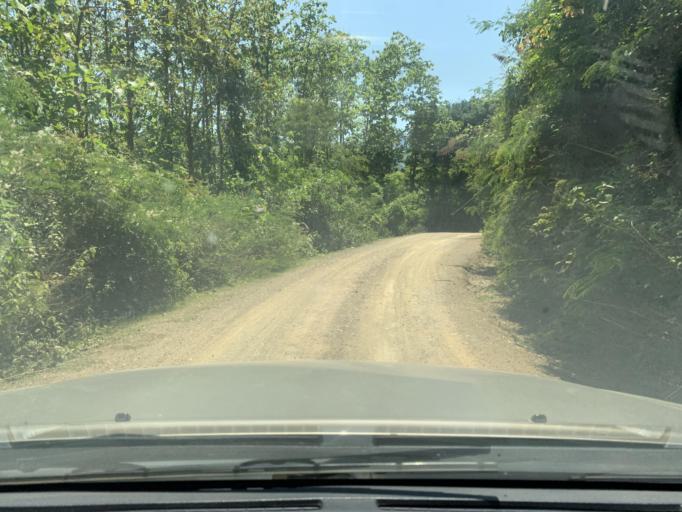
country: LA
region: Louangphabang
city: Louangphabang
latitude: 19.9053
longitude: 102.2245
